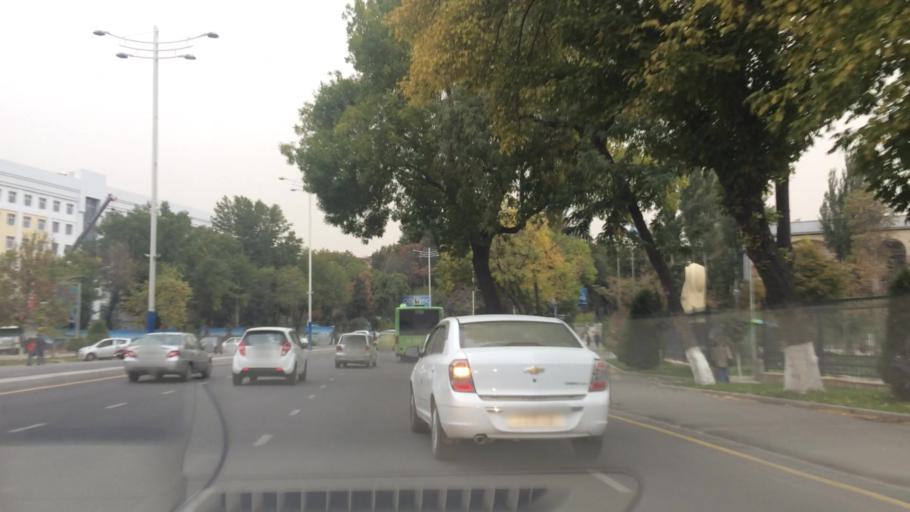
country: UZ
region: Toshkent Shahri
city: Tashkent
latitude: 41.3072
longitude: 69.2966
